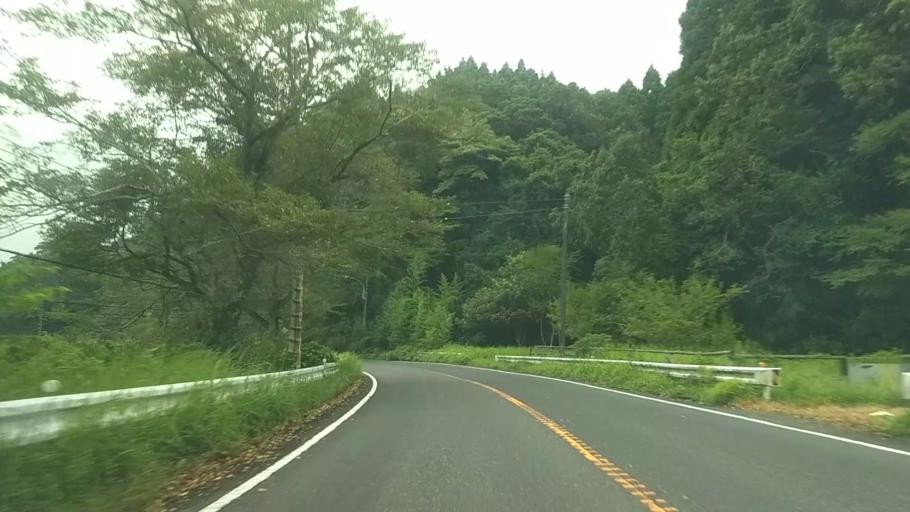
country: JP
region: Chiba
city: Kawaguchi
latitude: 35.2415
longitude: 140.0716
